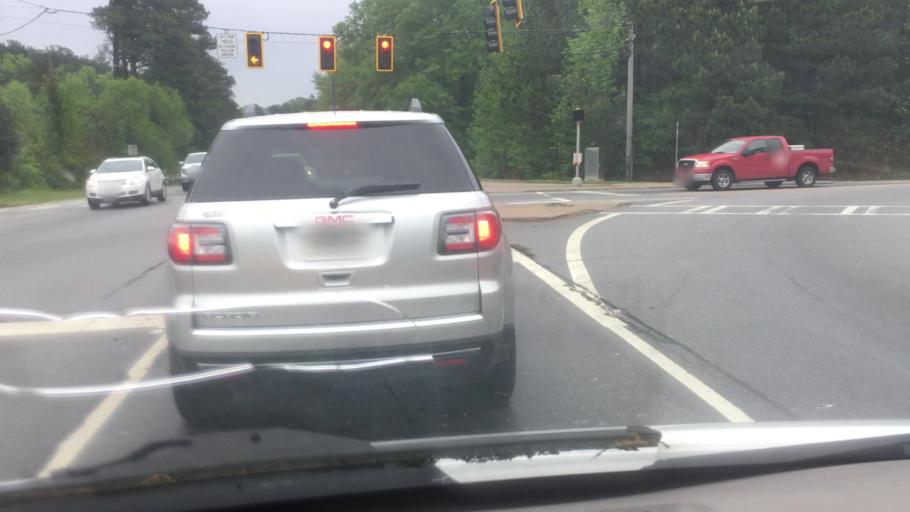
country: US
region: Georgia
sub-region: Paulding County
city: Dallas
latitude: 33.9182
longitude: -84.8284
